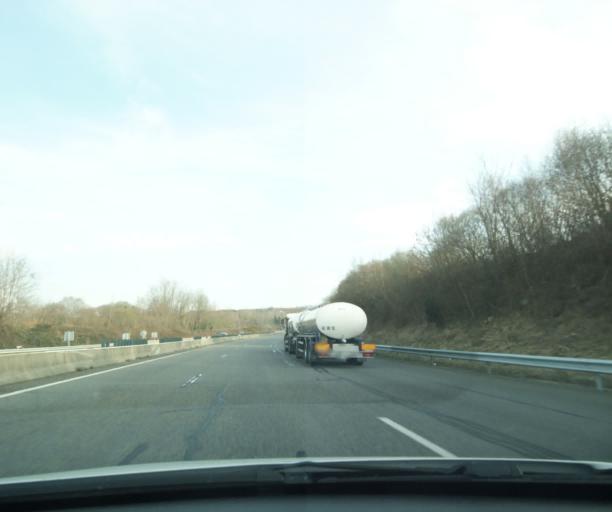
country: FR
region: Midi-Pyrenees
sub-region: Departement des Hautes-Pyrenees
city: Capvern
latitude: 43.1065
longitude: 0.3329
